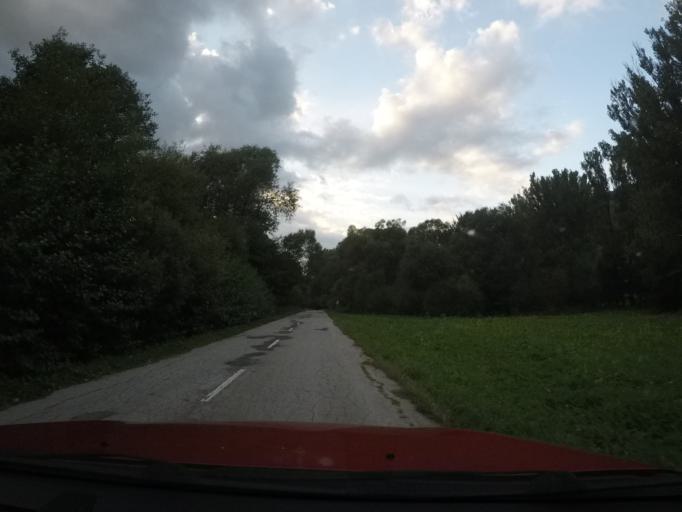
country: SK
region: Kosicky
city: Medzev
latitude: 48.6295
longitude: 20.7377
